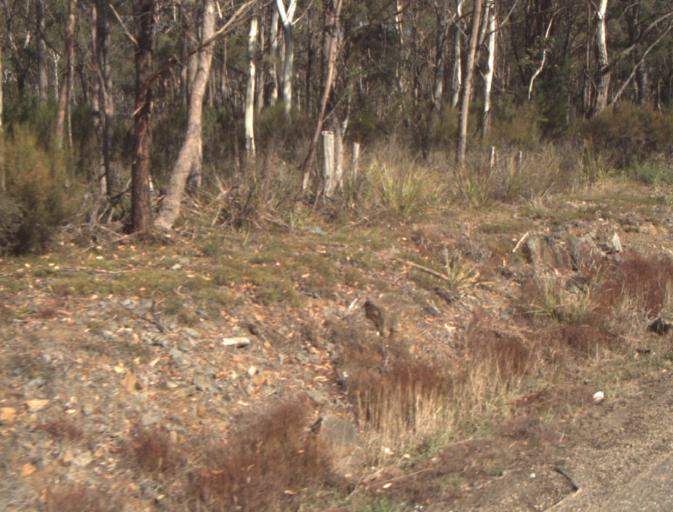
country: AU
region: Tasmania
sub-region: Launceston
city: Mayfield
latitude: -41.3165
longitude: 147.1934
